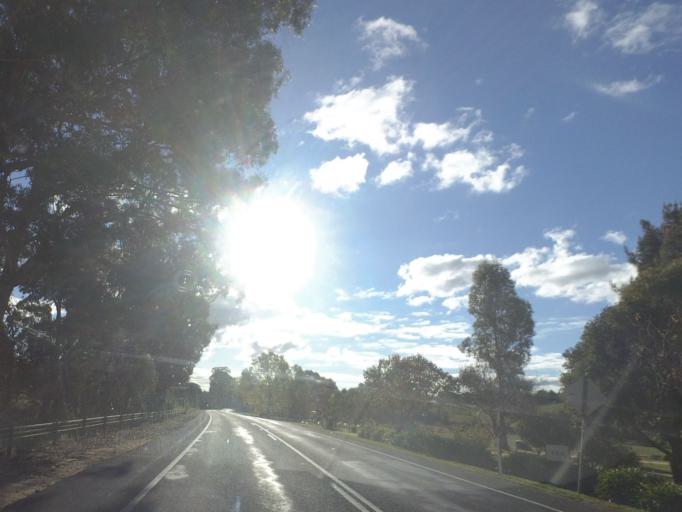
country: AU
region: Victoria
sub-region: Mount Alexander
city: Castlemaine
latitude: -37.0939
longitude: 144.2879
